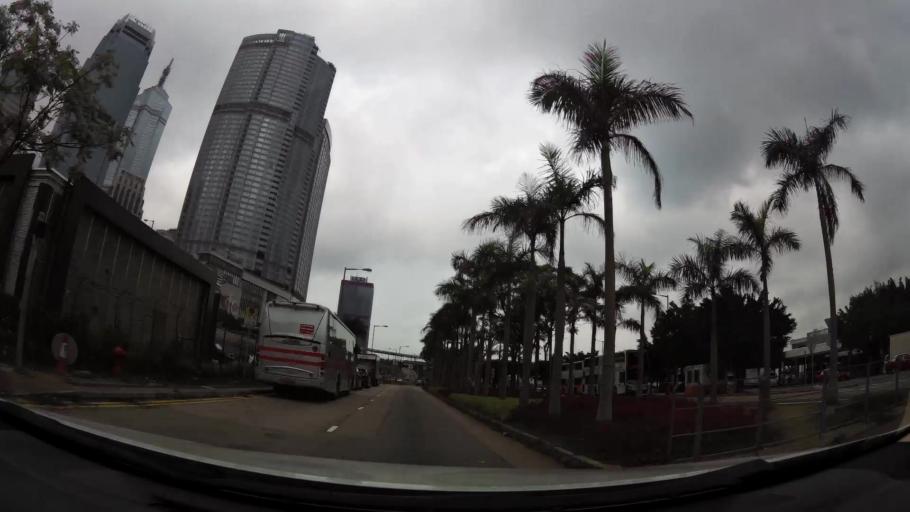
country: HK
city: Hong Kong
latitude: 22.2866
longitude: 114.1596
